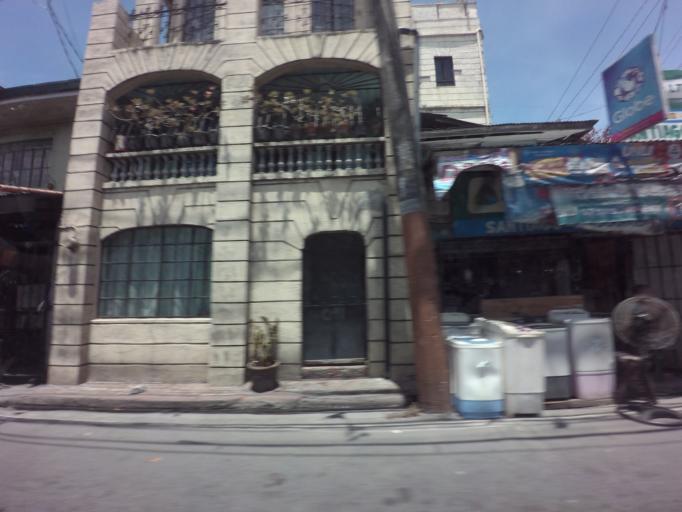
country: PH
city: Sambayanihan People's Village
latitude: 14.4837
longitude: 120.9841
